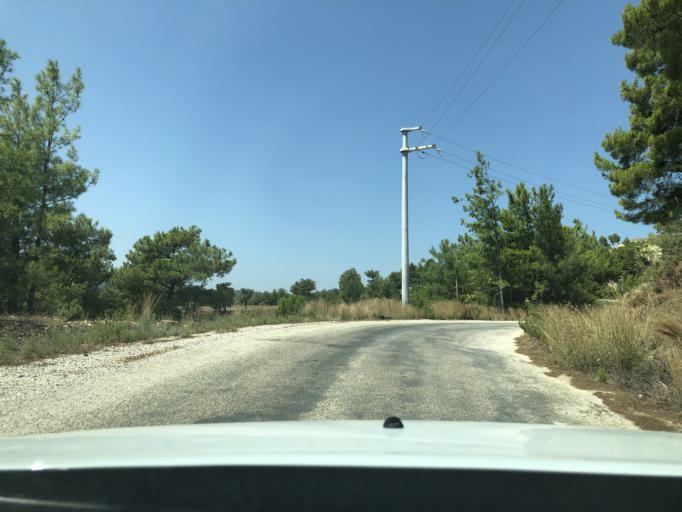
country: TR
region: Antalya
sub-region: Manavgat
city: Kizilagac
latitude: 36.8687
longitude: 31.5565
